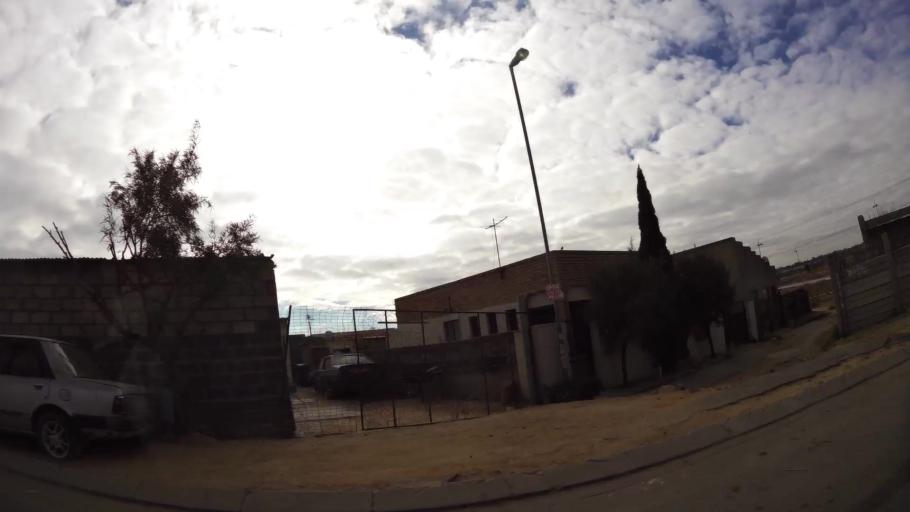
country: ZA
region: Gauteng
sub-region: City of Johannesburg Metropolitan Municipality
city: Modderfontein
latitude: -26.0521
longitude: 28.1836
